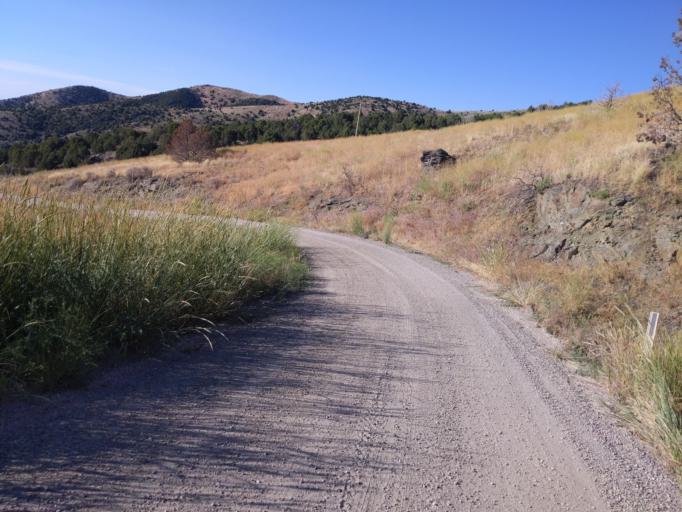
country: US
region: Idaho
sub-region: Bannock County
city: Pocatello
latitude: 42.8511
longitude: -112.3773
